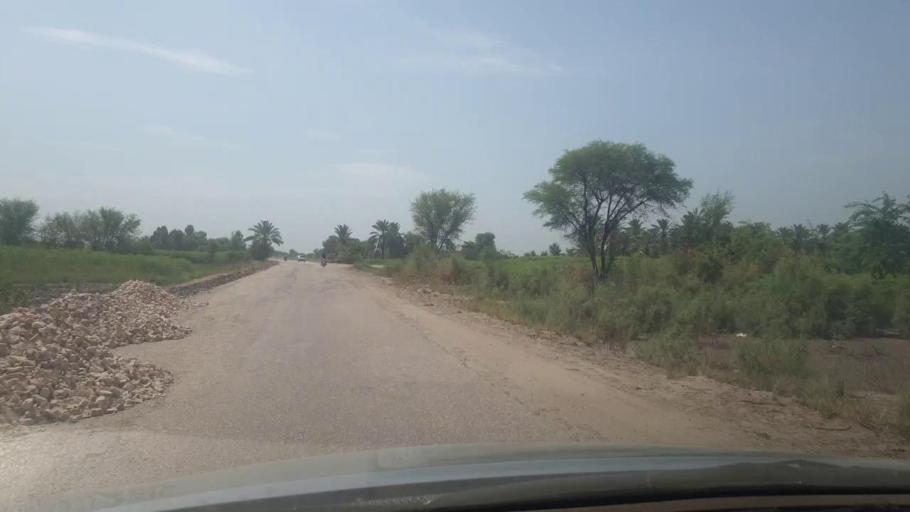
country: PK
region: Sindh
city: Bozdar
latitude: 27.2210
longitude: 68.5670
